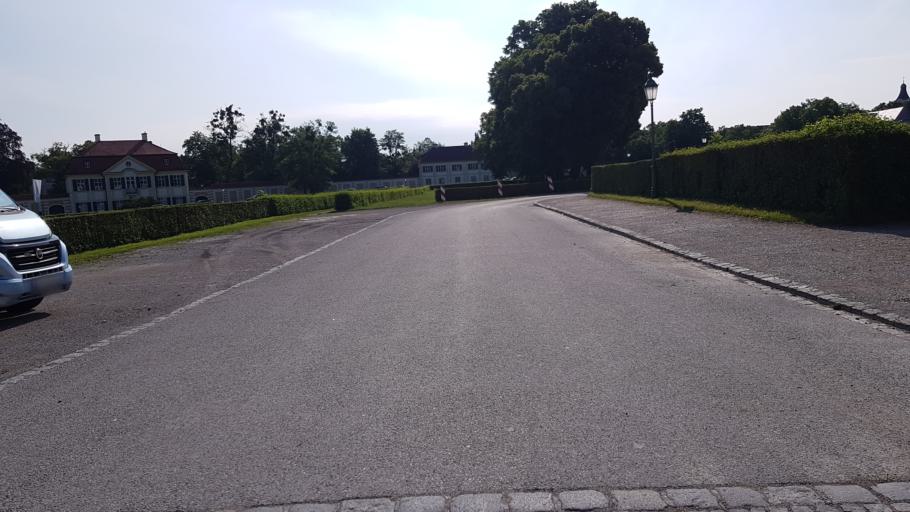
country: DE
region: Bavaria
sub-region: Upper Bavaria
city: Pasing
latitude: 48.1590
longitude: 11.5065
